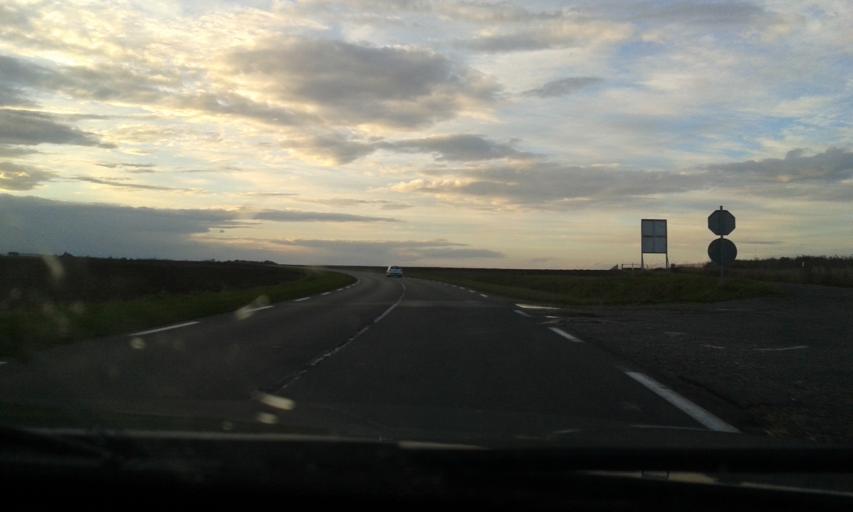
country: FR
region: Centre
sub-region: Departement du Loiret
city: Bricy
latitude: 47.9768
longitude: 1.7640
